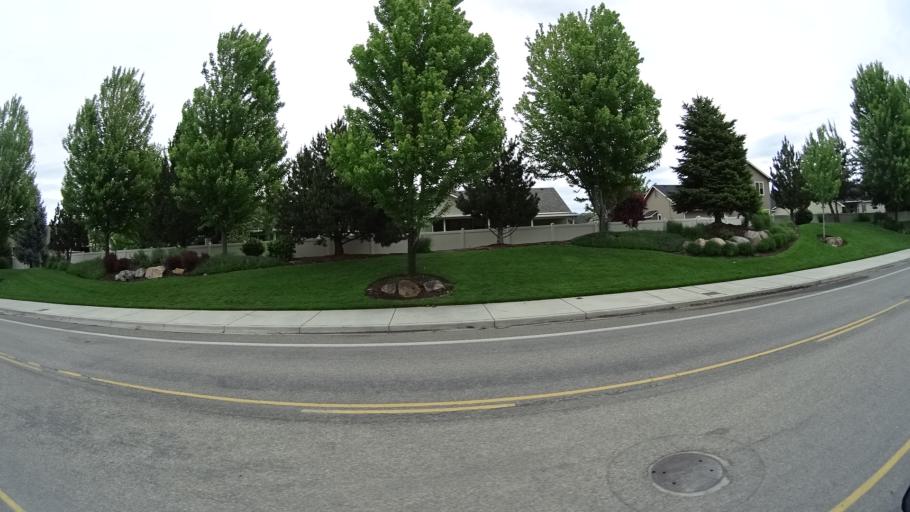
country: US
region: Idaho
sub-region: Ada County
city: Star
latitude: 43.7036
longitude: -116.4933
